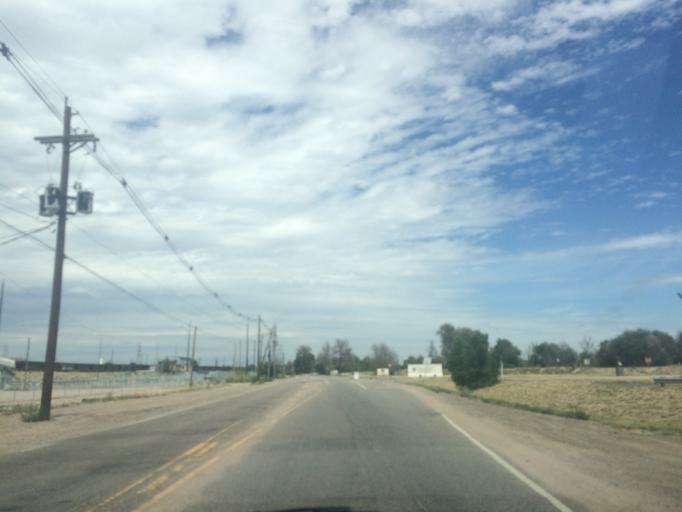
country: US
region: Colorado
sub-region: Adams County
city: Commerce City
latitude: 39.8043
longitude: -104.9593
